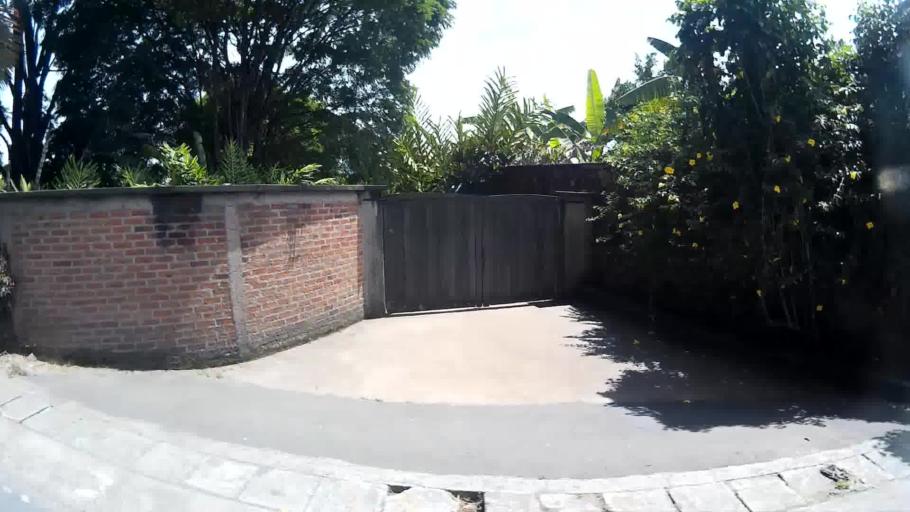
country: CO
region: Valle del Cauca
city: Cartago
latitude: 4.8034
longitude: -75.8255
